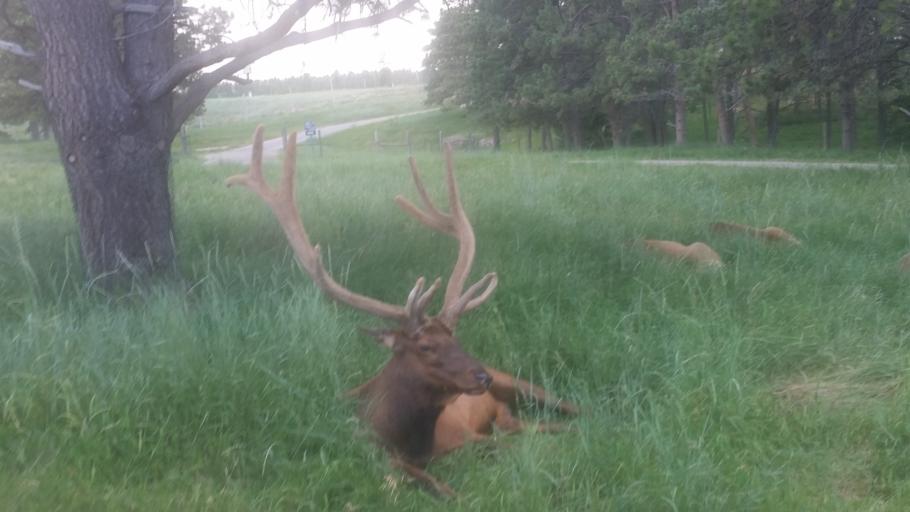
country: US
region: South Dakota
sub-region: Pennington County
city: Colonial Pine Hills
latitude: 43.9778
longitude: -103.2950
